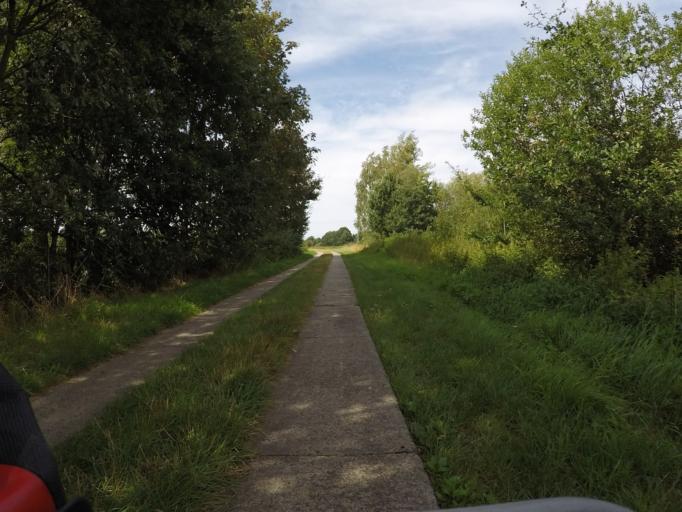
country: DE
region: Lower Saxony
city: Drage
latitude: 53.3685
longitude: 10.2775
